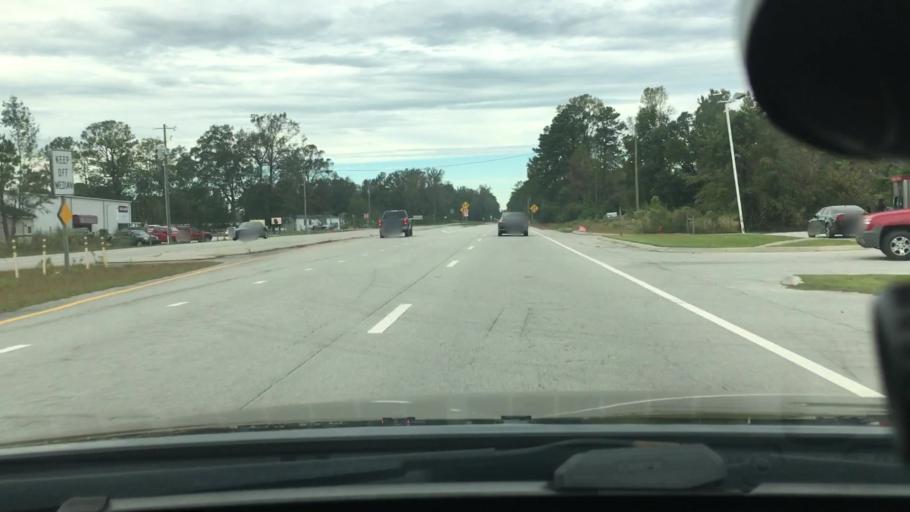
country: US
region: North Carolina
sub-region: Craven County
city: New Bern
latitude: 35.1549
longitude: -77.0358
